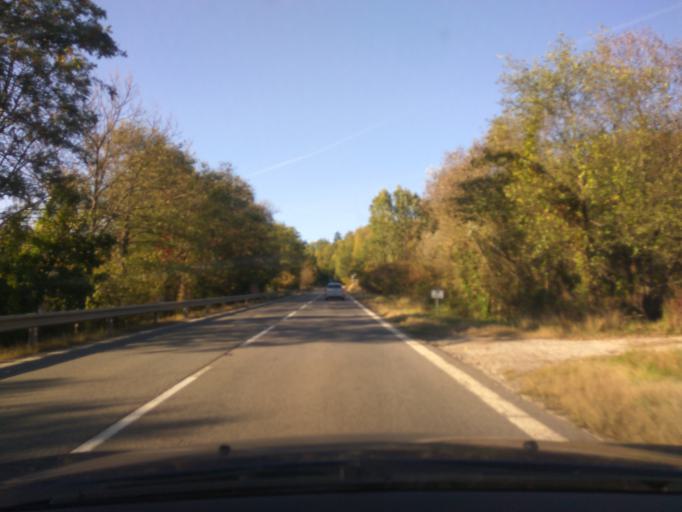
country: SK
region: Banskobystricky
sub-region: Okres Ziar nad Hronom
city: Kremnica
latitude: 48.6884
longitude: 18.9166
